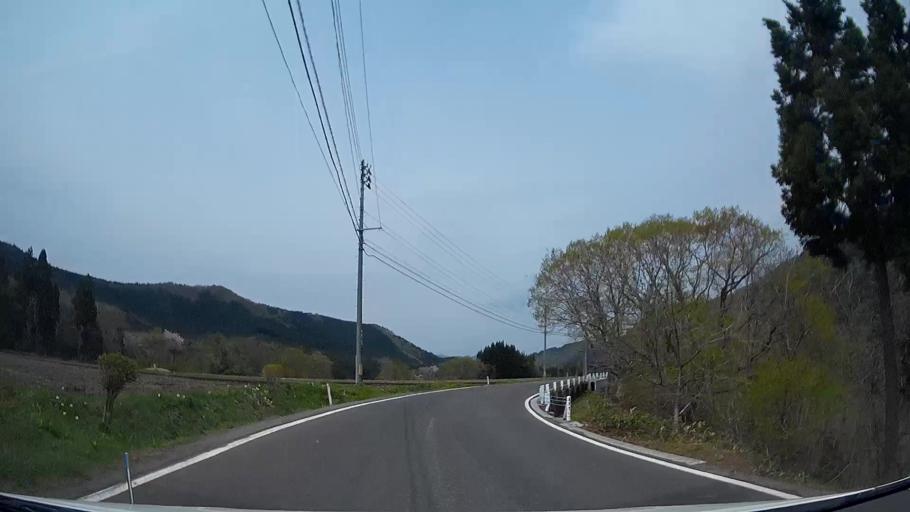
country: JP
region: Akita
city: Hanawa
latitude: 40.0567
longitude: 140.8126
